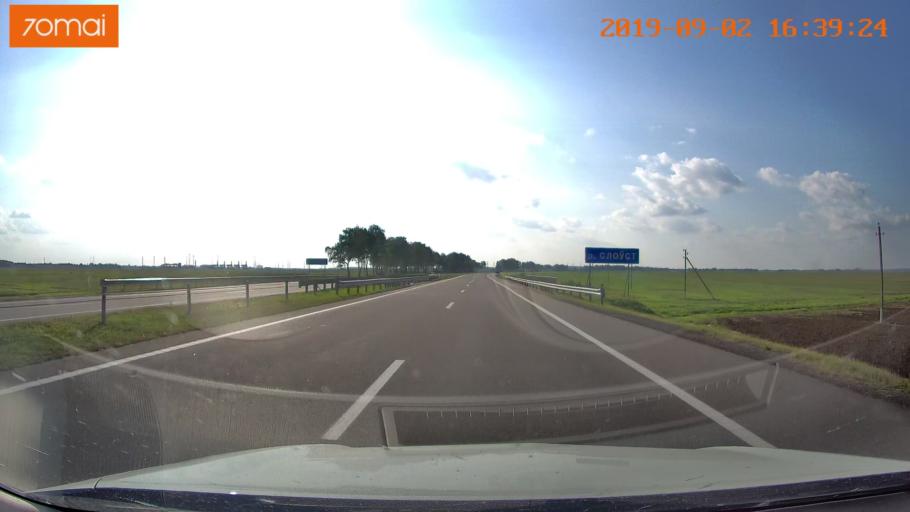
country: BY
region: Minsk
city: Luhavaya Slabada
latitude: 53.7638
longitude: 27.8805
